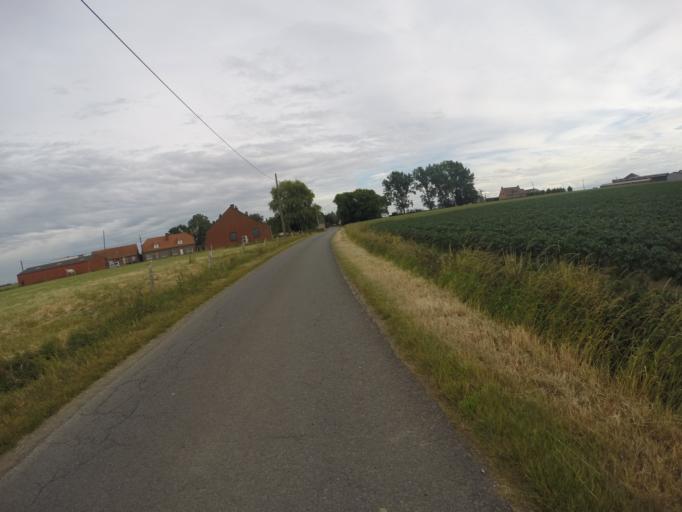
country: BE
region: Flanders
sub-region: Provincie West-Vlaanderen
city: Ruiselede
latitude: 51.0103
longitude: 3.3908
